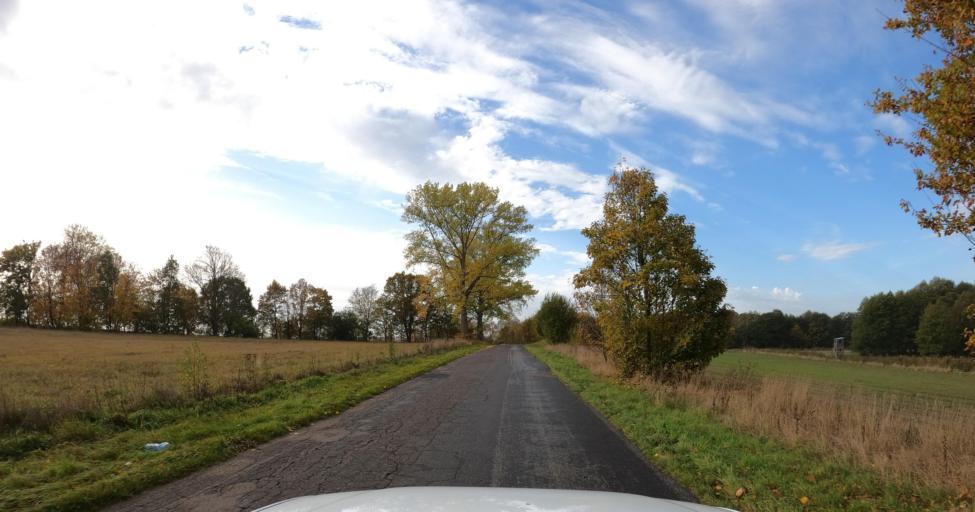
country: PL
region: West Pomeranian Voivodeship
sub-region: Powiat kamienski
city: Kamien Pomorski
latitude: 53.9613
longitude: 14.8155
